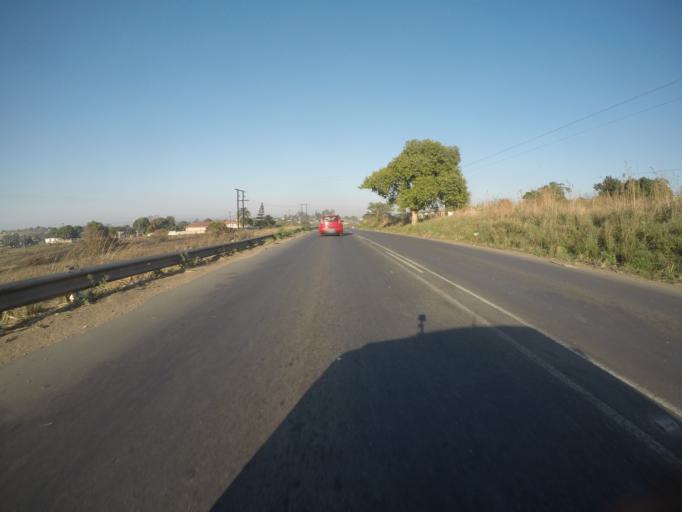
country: ZA
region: KwaZulu-Natal
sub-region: iLembe District Municipality
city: Stanger
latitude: -29.4094
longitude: 31.2465
